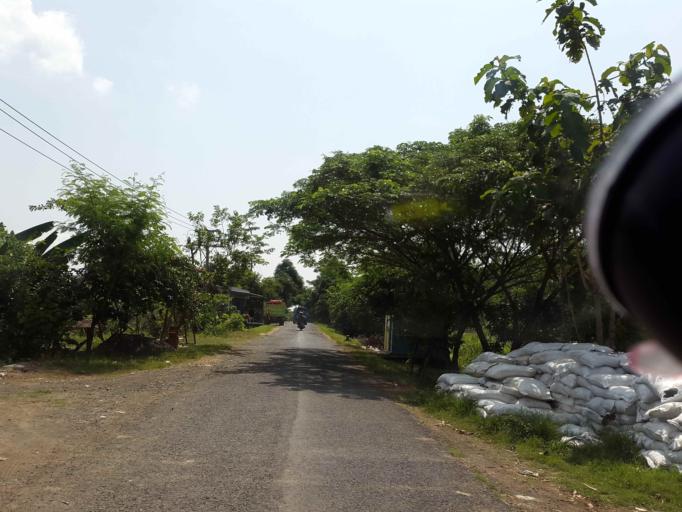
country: ID
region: Central Java
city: Pemalang
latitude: -6.9514
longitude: 109.3626
